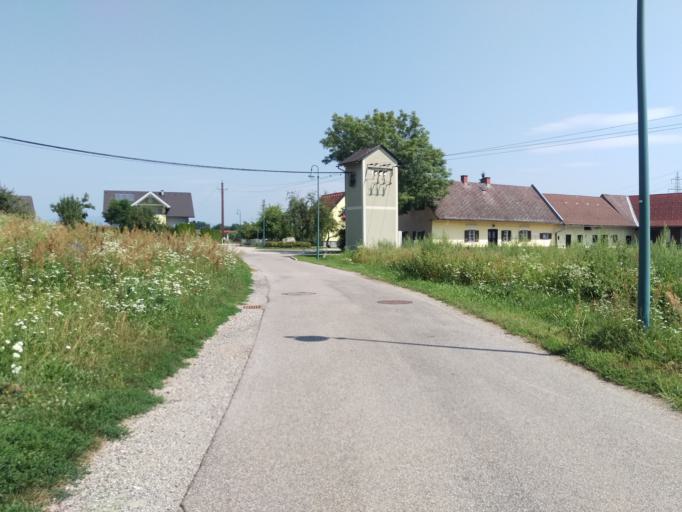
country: AT
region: Styria
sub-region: Politischer Bezirk Graz-Umgebung
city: Kalsdorf bei Graz
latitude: 46.9457
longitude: 15.4883
